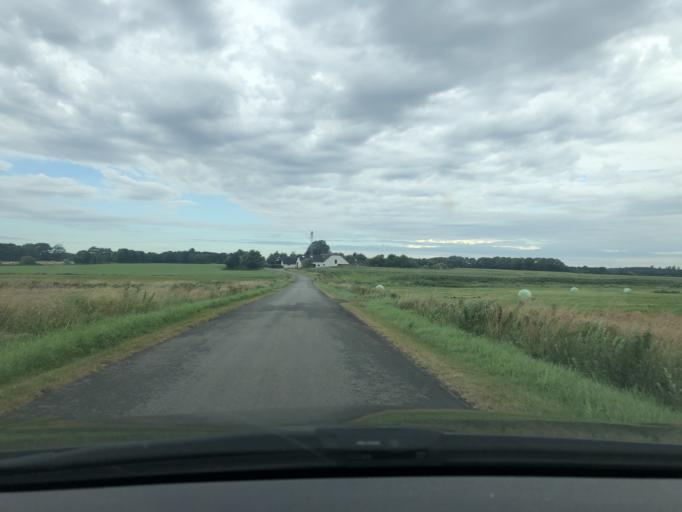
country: DK
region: South Denmark
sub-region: Varde Kommune
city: Olgod
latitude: 55.8077
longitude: 8.6907
